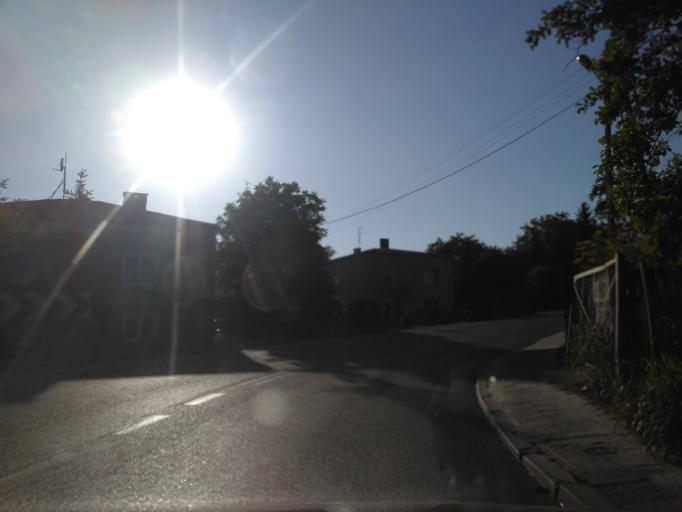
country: PL
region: Lublin Voivodeship
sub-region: Powiat lubelski
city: Bychawa
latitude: 51.0174
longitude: 22.5253
